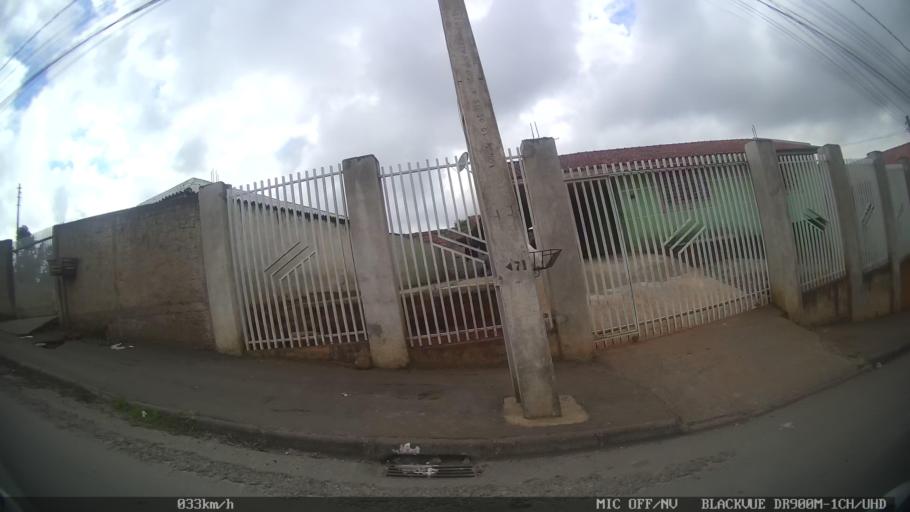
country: BR
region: Parana
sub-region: Colombo
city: Colombo
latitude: -25.3427
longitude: -49.2388
